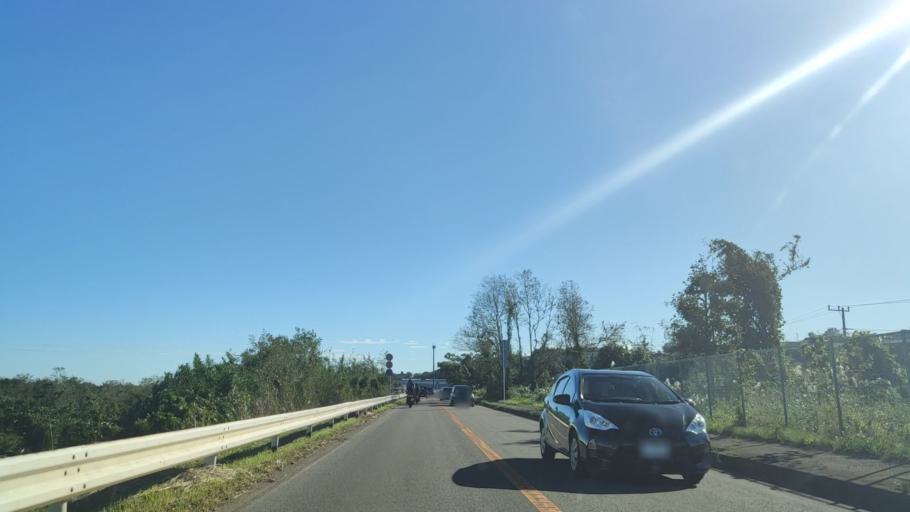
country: JP
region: Kanagawa
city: Zama
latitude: 35.4998
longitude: 139.3714
